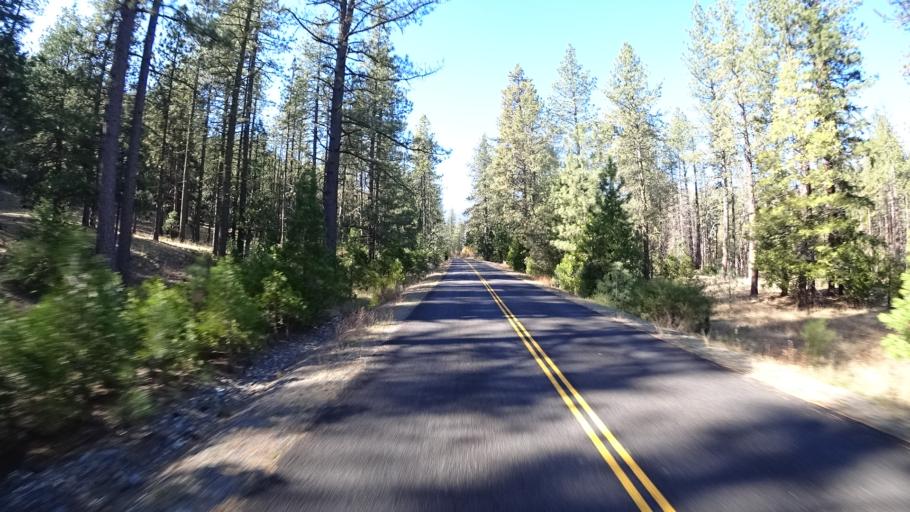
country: US
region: California
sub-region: Siskiyou County
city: Weed
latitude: 41.4340
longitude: -122.4760
